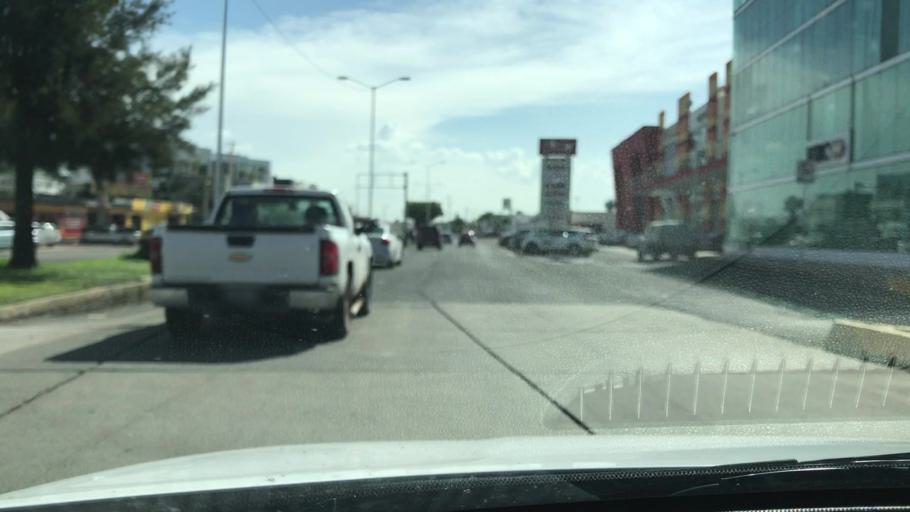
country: MX
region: Guanajuato
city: Celaya
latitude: 20.5176
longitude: -100.7899
